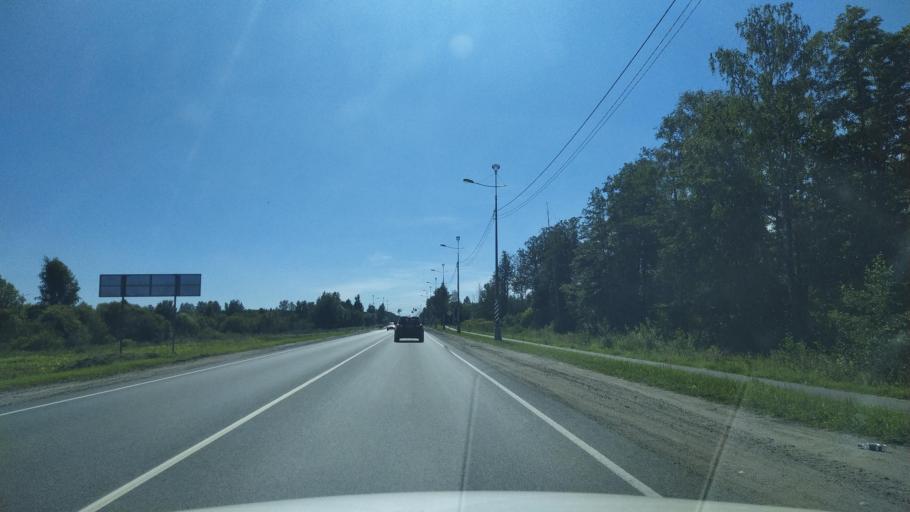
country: RU
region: Pskov
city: Pskov
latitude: 57.7927
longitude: 28.4148
